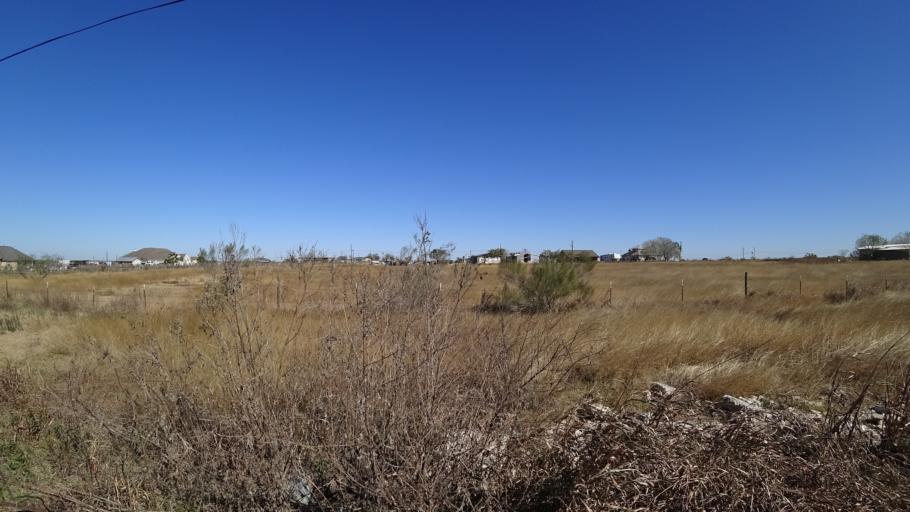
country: US
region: Texas
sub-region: Travis County
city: Garfield
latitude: 30.0988
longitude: -97.6188
